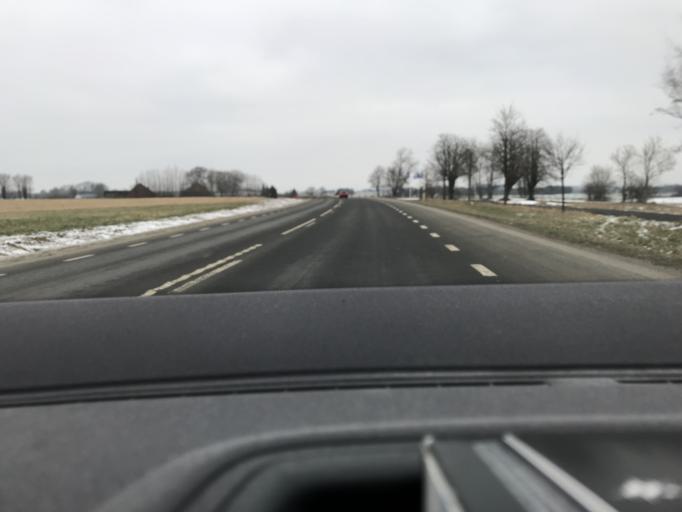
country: SE
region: Skane
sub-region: Ystads Kommun
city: Ystad
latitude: 55.4526
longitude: 13.8484
